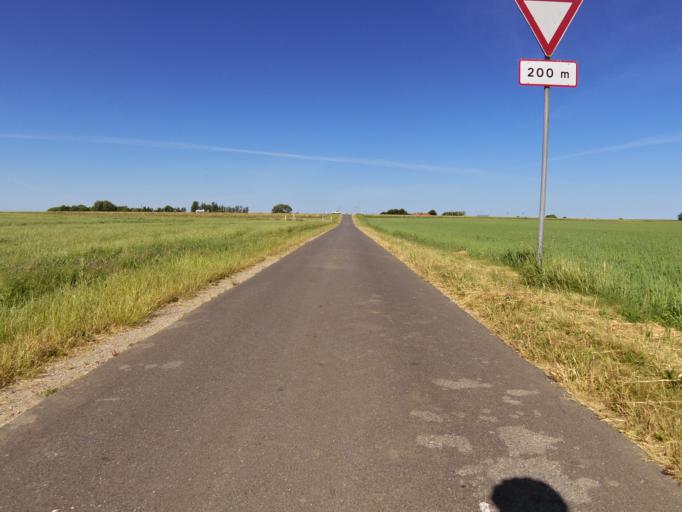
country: DK
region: Central Jutland
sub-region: Struer Kommune
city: Struer
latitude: 56.4637
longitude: 8.5922
